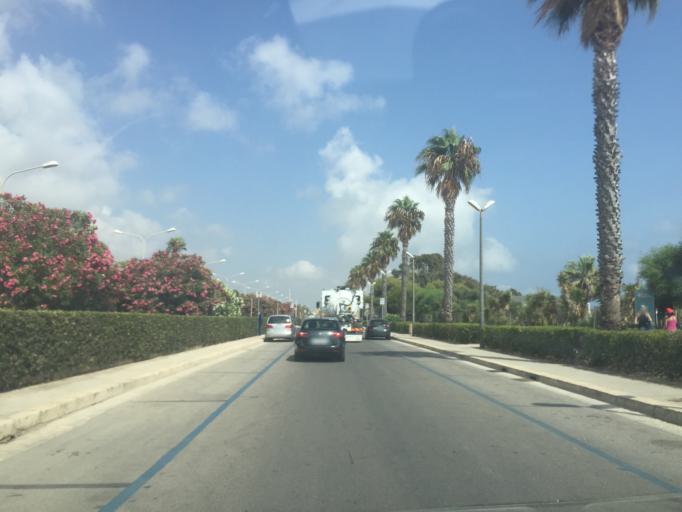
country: IT
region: Sicily
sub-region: Ragusa
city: Marina di Ragusa
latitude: 36.7812
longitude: 14.5656
